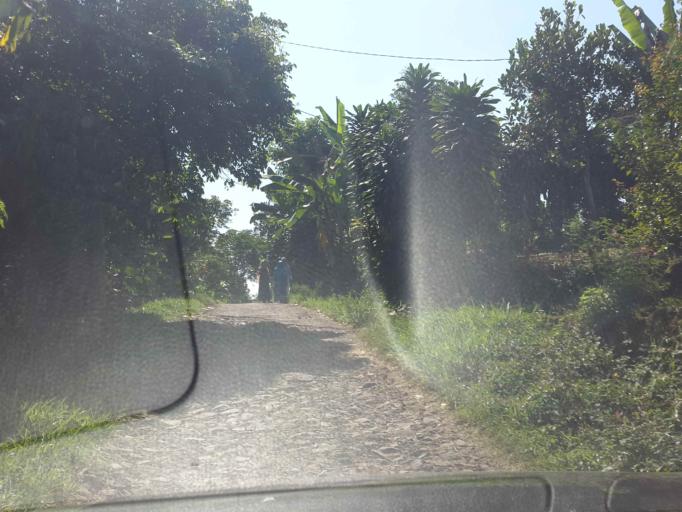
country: ID
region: West Java
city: Ciranjang-hilir
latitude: -6.7560
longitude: 107.1356
